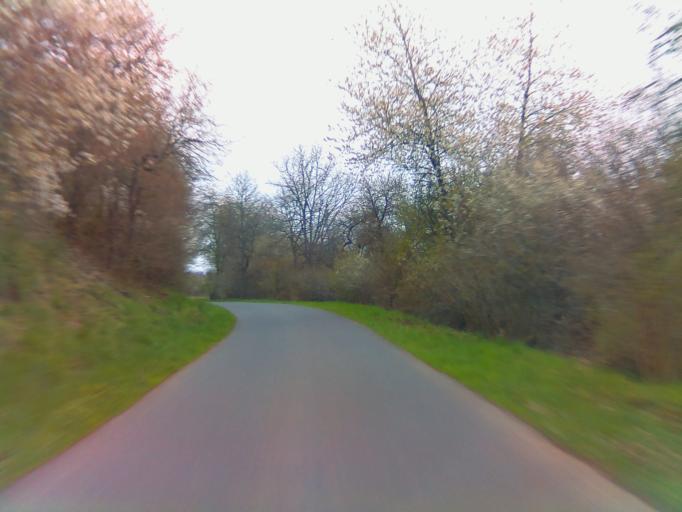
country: DE
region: Rheinland-Pfalz
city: Hoppstadten-Weiersbach
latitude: 49.6203
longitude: 7.2053
